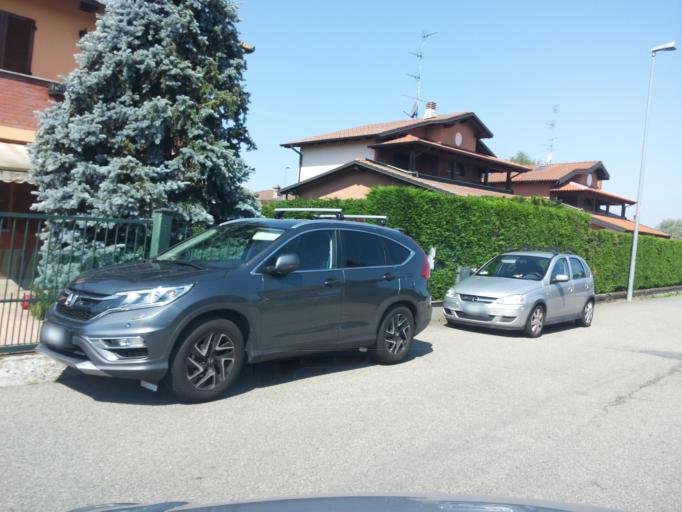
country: IT
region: Piedmont
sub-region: Provincia di Vercelli
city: Borgo Vercelli
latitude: 45.3598
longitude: 8.4663
